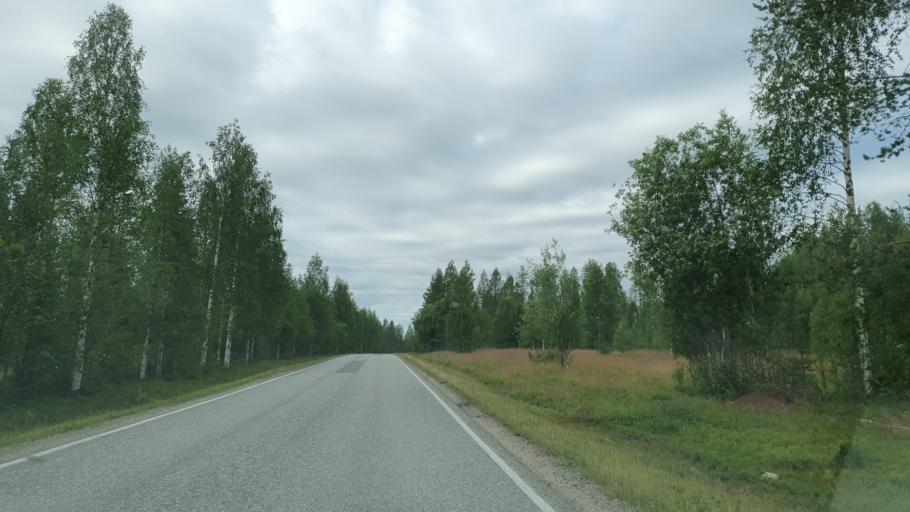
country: FI
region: Lapland
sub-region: Tunturi-Lappi
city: Kittilae
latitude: 67.6089
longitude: 25.2815
